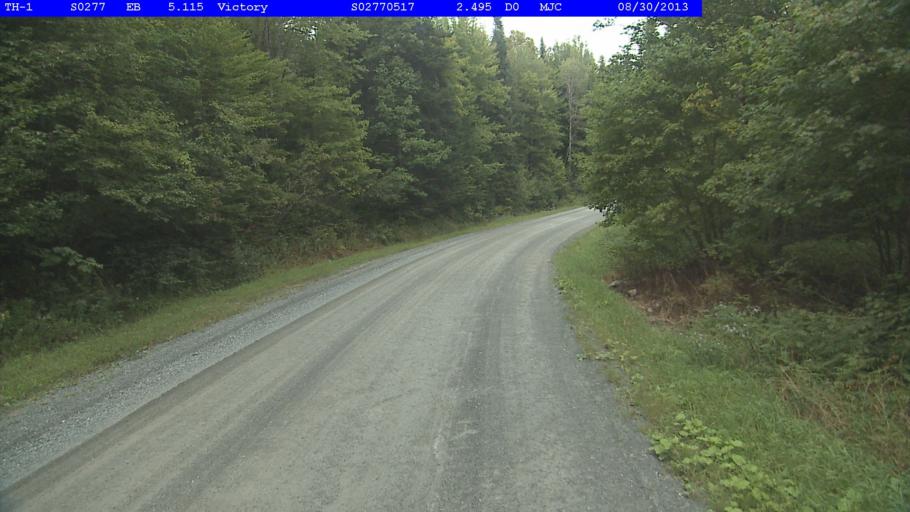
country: US
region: Vermont
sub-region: Caledonia County
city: Lyndonville
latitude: 44.5209
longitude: -71.8219
